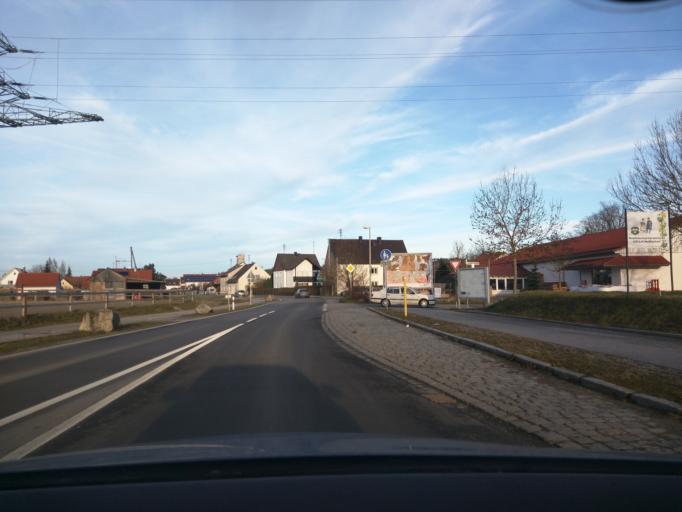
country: DE
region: Bavaria
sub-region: Upper Bavaria
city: Au in der Hallertau
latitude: 48.5546
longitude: 11.7336
